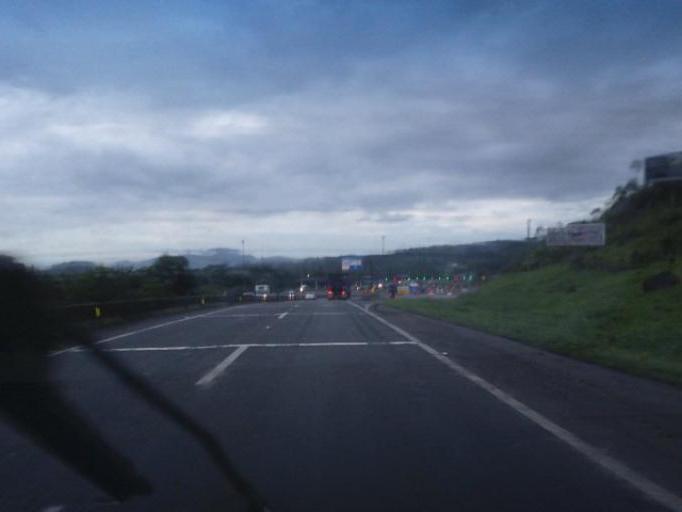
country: BR
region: Santa Catarina
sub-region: Joinville
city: Joinville
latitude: -25.9887
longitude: -48.8838
